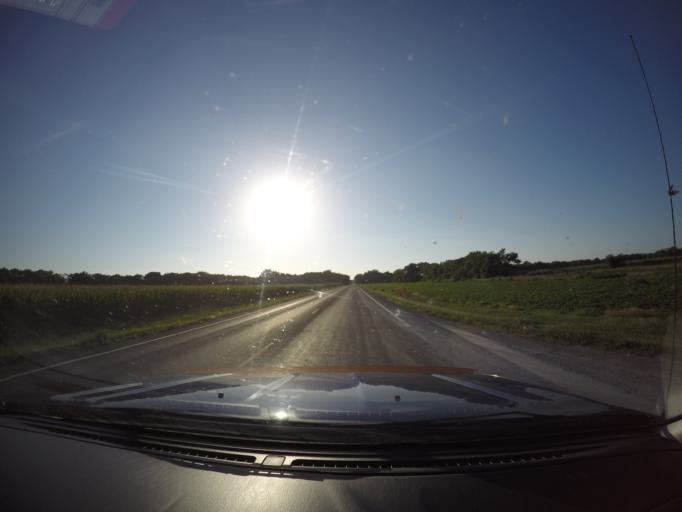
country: US
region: Kansas
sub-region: Pottawatomie County
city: Saint Marys
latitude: 39.2111
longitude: -96.1105
